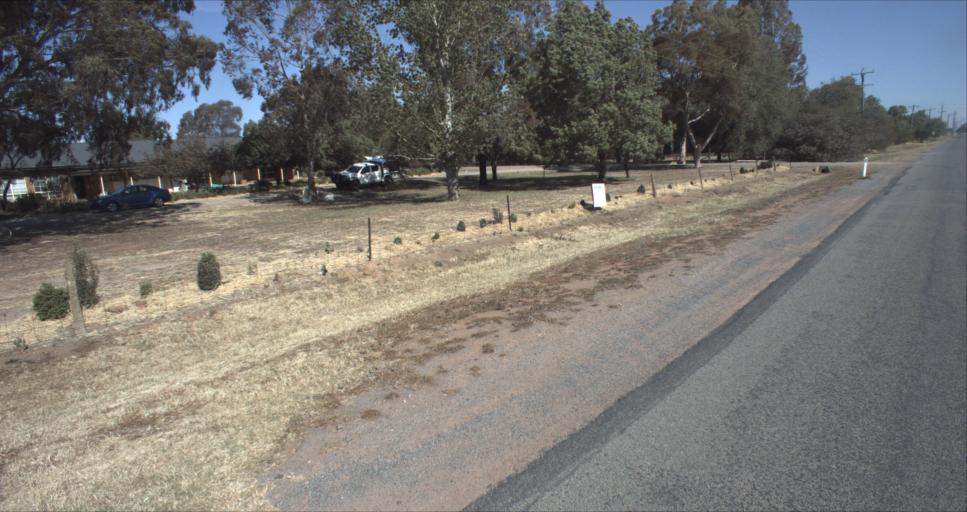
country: AU
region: New South Wales
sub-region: Leeton
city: Leeton
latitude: -34.5413
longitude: 146.4190
